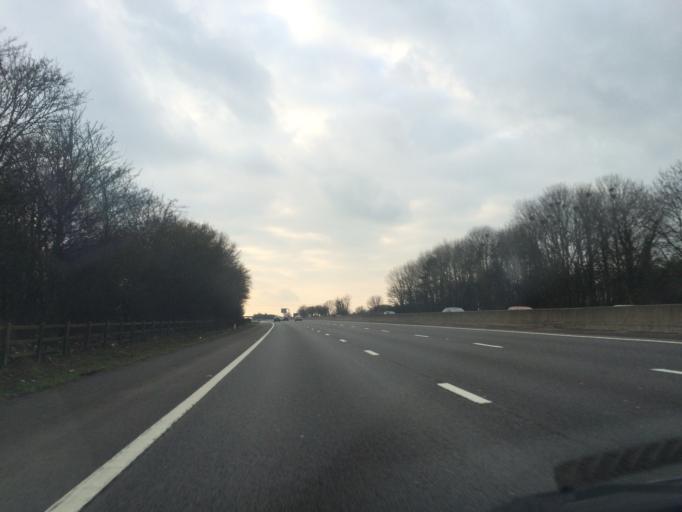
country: GB
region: England
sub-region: West Berkshire
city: Lambourn
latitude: 51.4827
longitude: -1.5585
